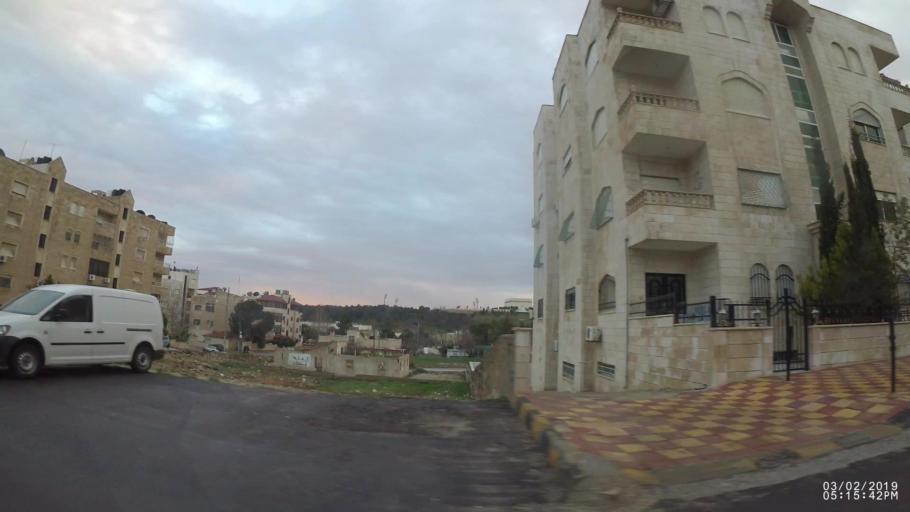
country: JO
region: Amman
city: Amman
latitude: 31.9861
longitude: 35.9119
